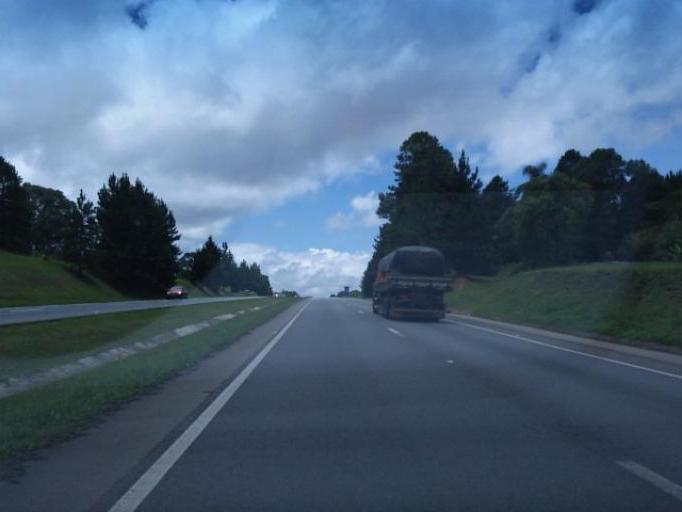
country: BR
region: Parana
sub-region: Piraquara
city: Piraquara
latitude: -25.4205
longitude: -49.0719
